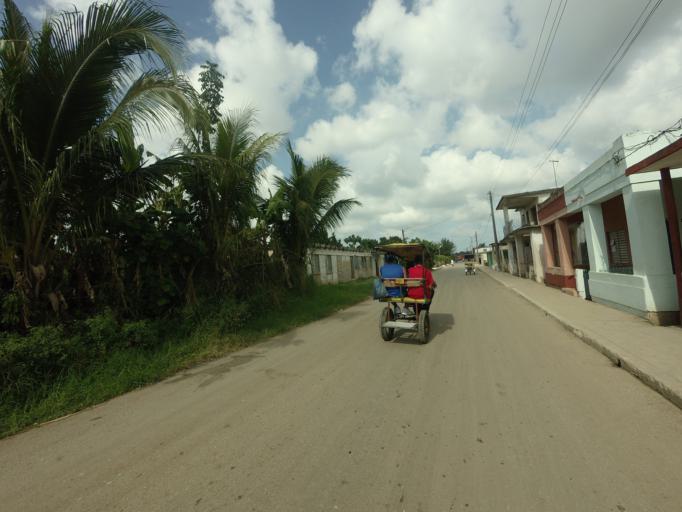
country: CU
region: Artemisa
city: Bauta
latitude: 22.9820
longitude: -82.5509
